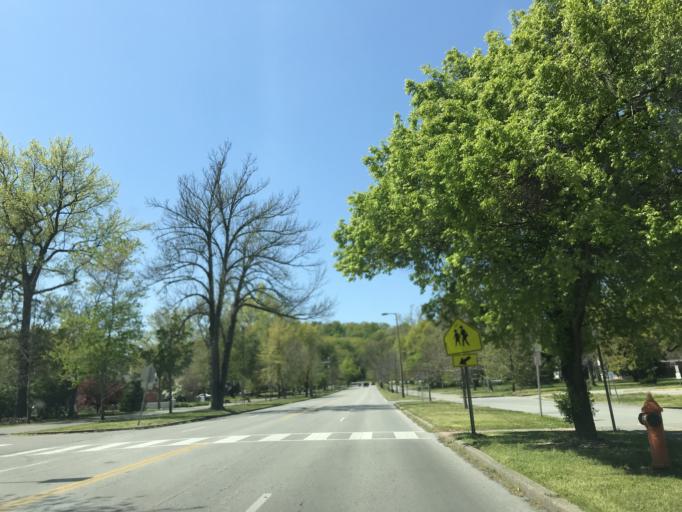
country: US
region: Kentucky
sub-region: Jefferson County
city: Shively
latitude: 38.1721
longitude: -85.7783
